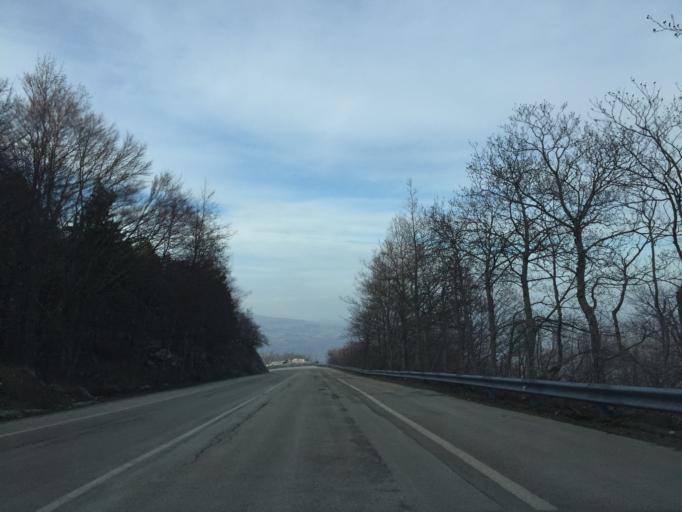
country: IT
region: Molise
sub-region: Provincia di Campobasso
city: San Massimo
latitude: 41.4724
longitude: 14.4146
